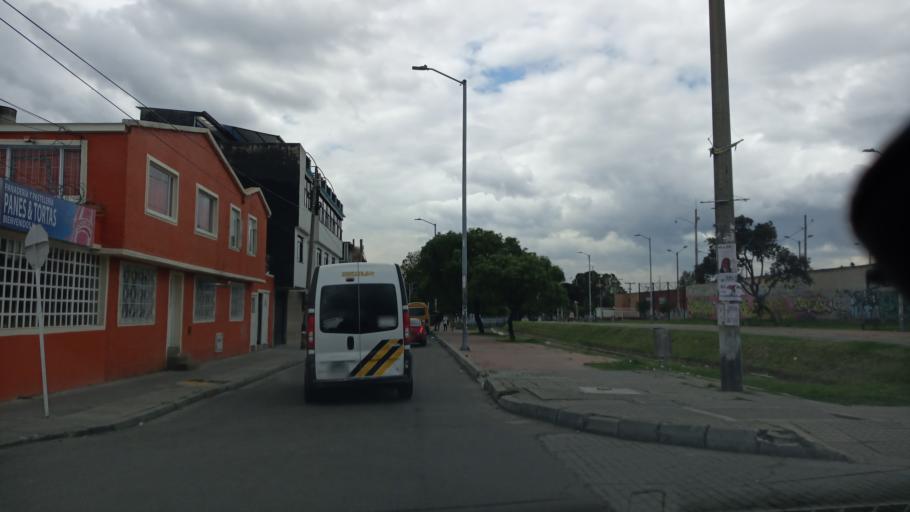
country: CO
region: Bogota D.C.
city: Bogota
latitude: 4.5755
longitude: -74.1090
